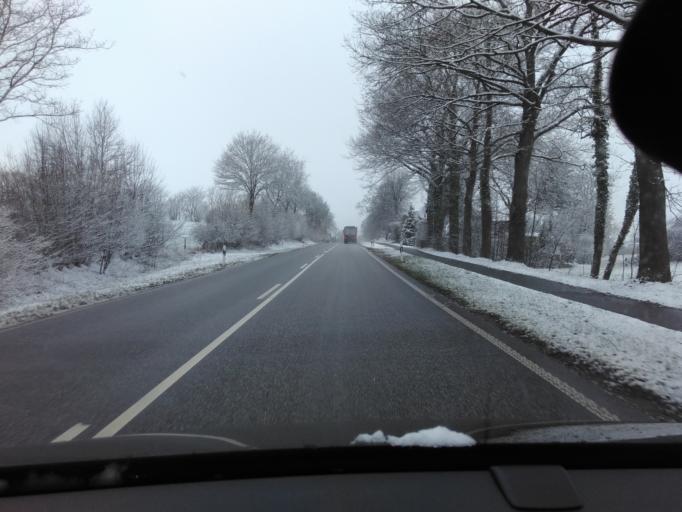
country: DE
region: Schleswig-Holstein
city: Glasau
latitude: 53.9992
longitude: 10.5019
